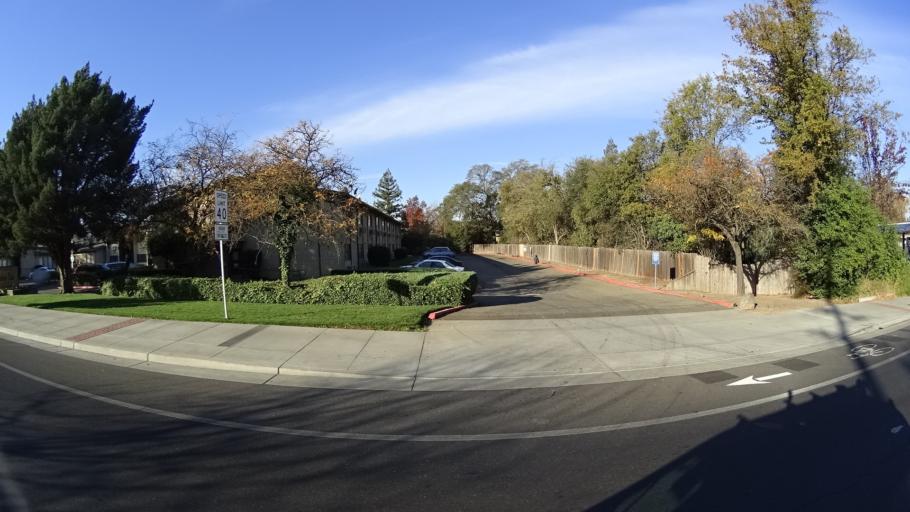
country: US
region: California
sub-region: Sacramento County
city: Citrus Heights
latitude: 38.7027
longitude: -121.2719
